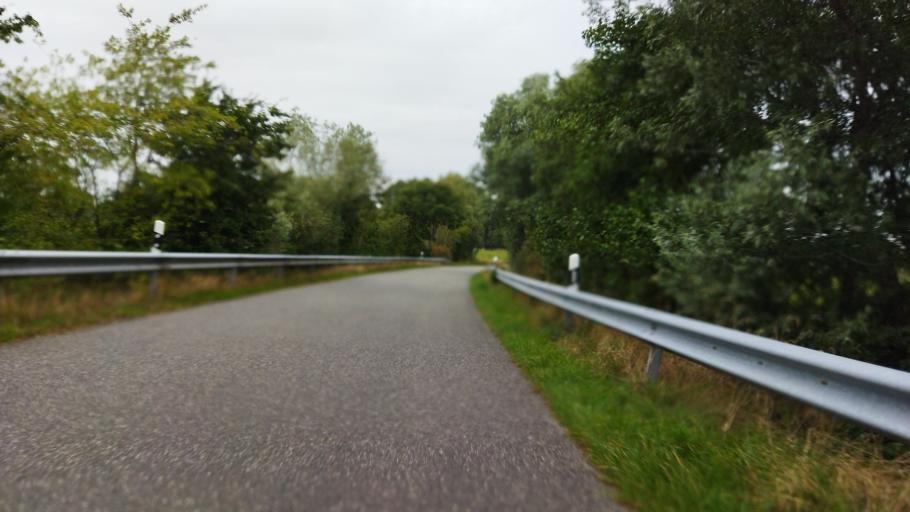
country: DE
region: Lower Saxony
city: Leer
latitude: 53.2568
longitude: 7.4375
